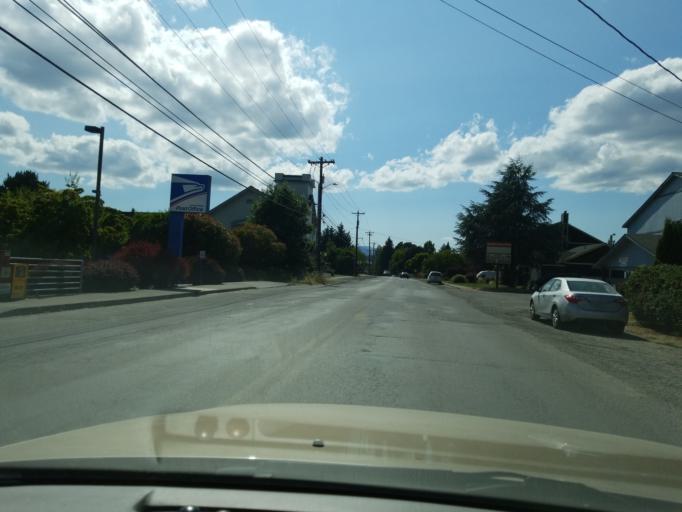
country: US
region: Oregon
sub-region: Yamhill County
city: Carlton
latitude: 45.2943
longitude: -123.1801
